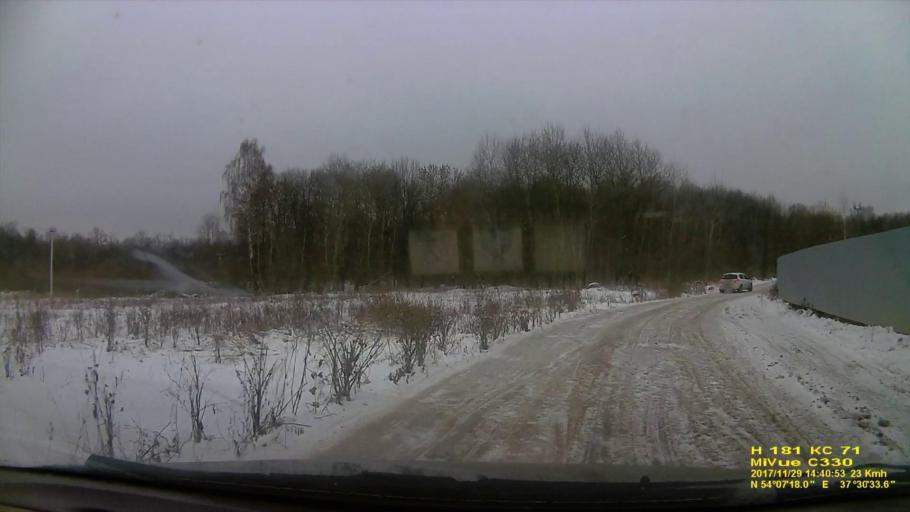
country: RU
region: Tula
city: Kosaya Gora
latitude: 54.1220
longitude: 37.5092
